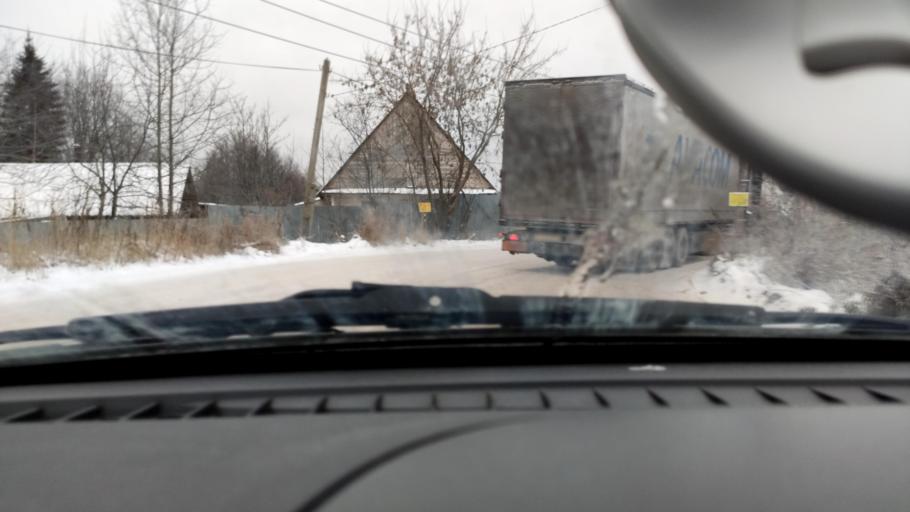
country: RU
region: Perm
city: Polazna
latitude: 58.1786
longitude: 56.4116
